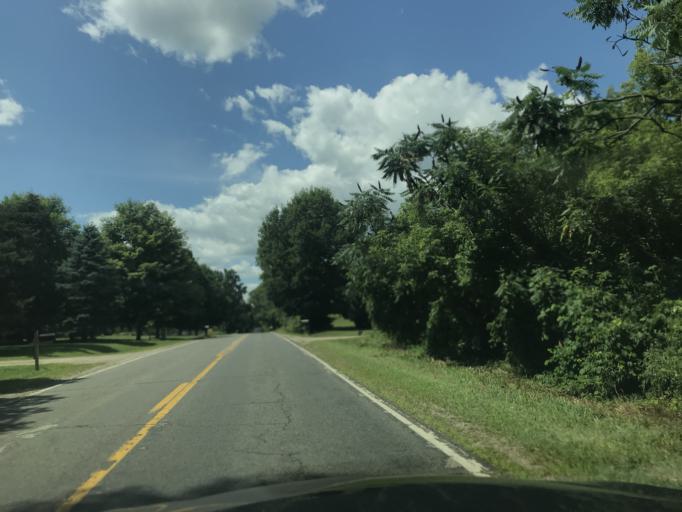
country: US
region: Michigan
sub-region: Ingham County
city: Leslie
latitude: 42.4511
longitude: -84.4918
